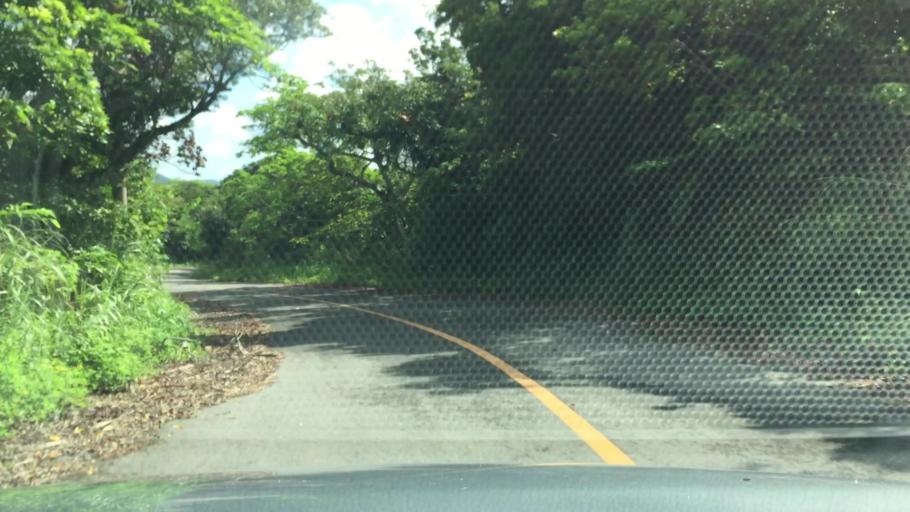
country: JP
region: Okinawa
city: Ishigaki
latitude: 24.3823
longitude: 124.1656
